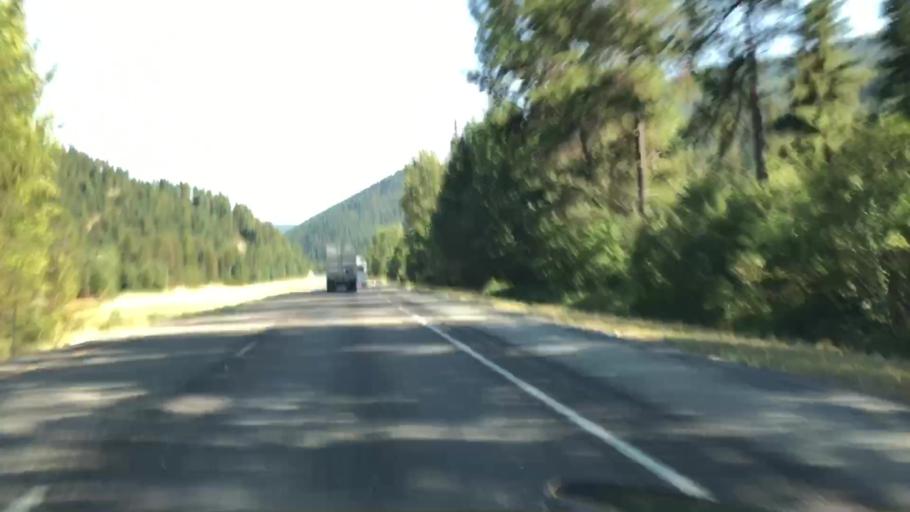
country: US
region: Montana
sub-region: Sanders County
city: Thompson Falls
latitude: 47.3657
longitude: -115.3295
